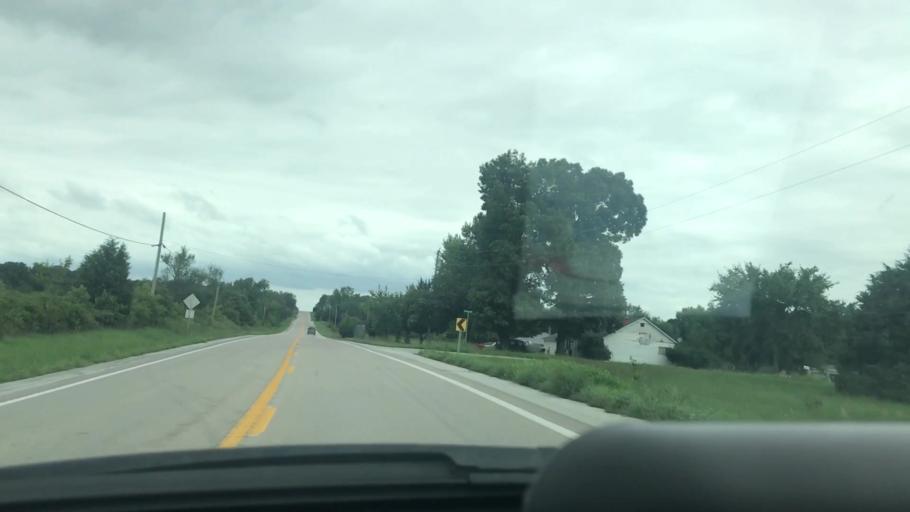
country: US
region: Missouri
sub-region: Dallas County
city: Buffalo
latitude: 37.6956
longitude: -93.1031
